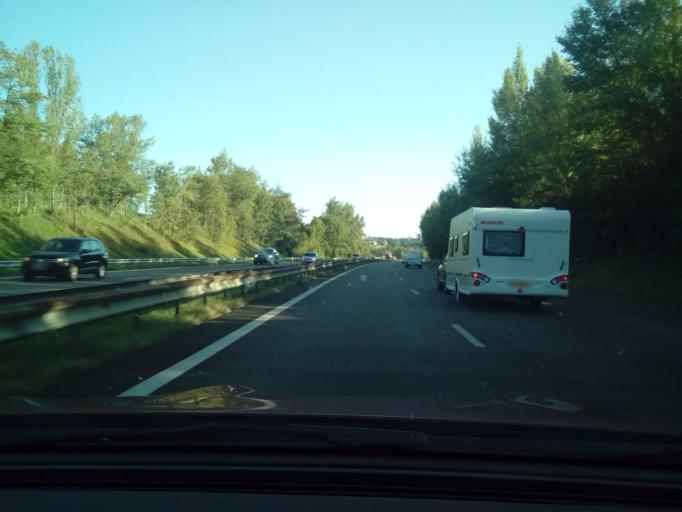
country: FR
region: Rhone-Alpes
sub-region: Departement de la Savoie
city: Gresy-sur-Aix
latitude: 45.7363
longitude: 5.9239
